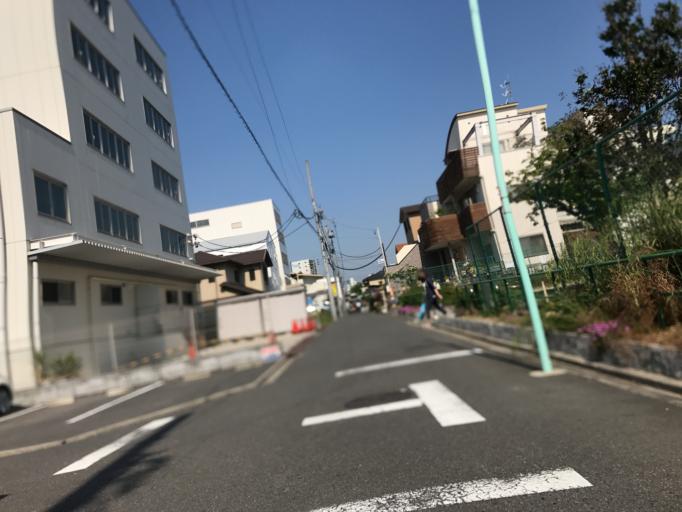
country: JP
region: Aichi
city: Nagoya-shi
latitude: 35.1762
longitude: 136.9285
